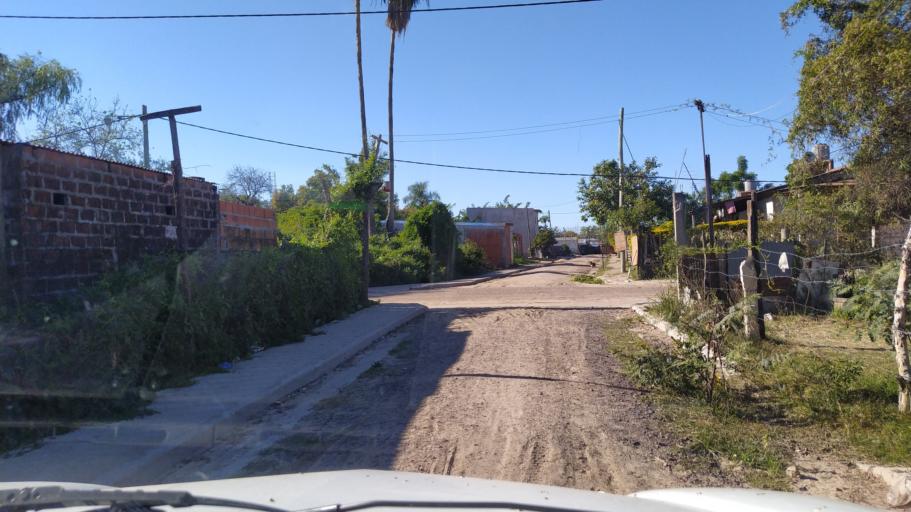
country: AR
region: Corrientes
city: Corrientes
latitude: -27.4954
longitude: -58.8031
